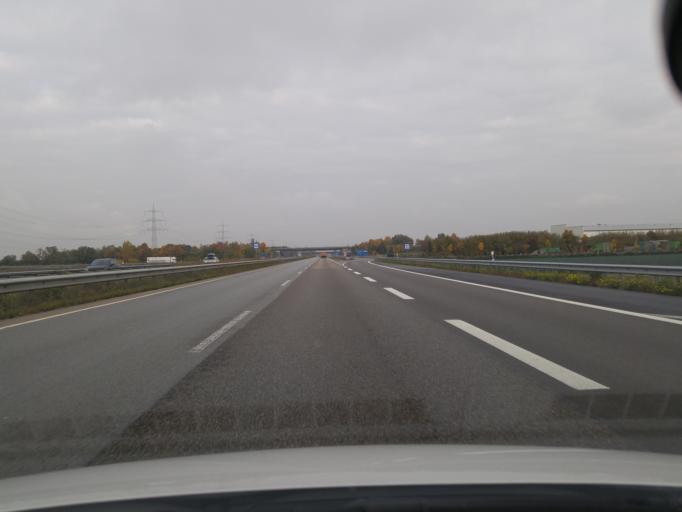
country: DE
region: Rheinland-Pfalz
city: Dannstadt-Schauernheim
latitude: 49.4336
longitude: 8.3308
